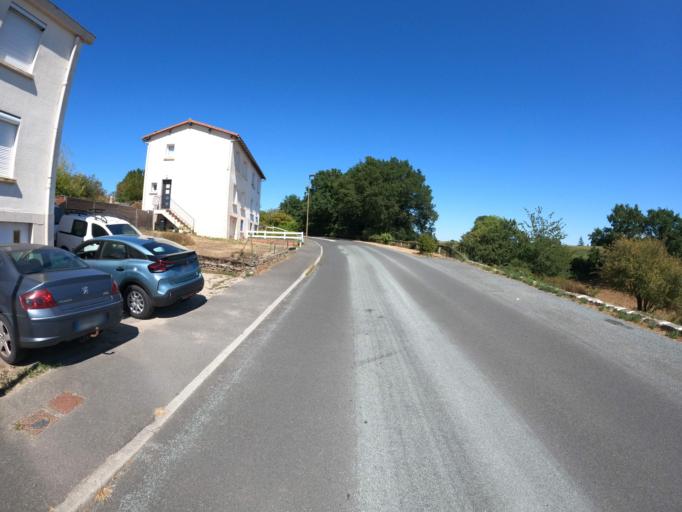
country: FR
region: Pays de la Loire
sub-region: Departement de la Vendee
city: Saint-Aubin-des-Ormeaux
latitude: 46.9896
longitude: -1.0451
